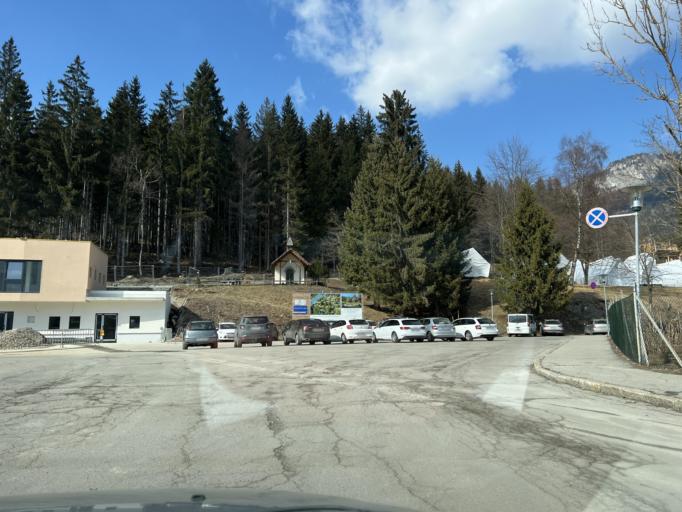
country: AT
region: Carinthia
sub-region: Politischer Bezirk Spittal an der Drau
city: Oberdrauburg
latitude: 46.6761
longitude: 12.9968
